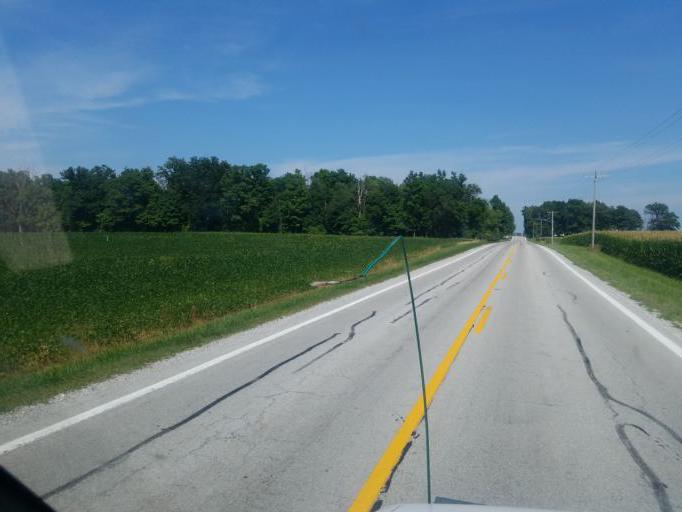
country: US
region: Ohio
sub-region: Shelby County
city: Botkins
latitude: 40.4967
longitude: -84.2232
